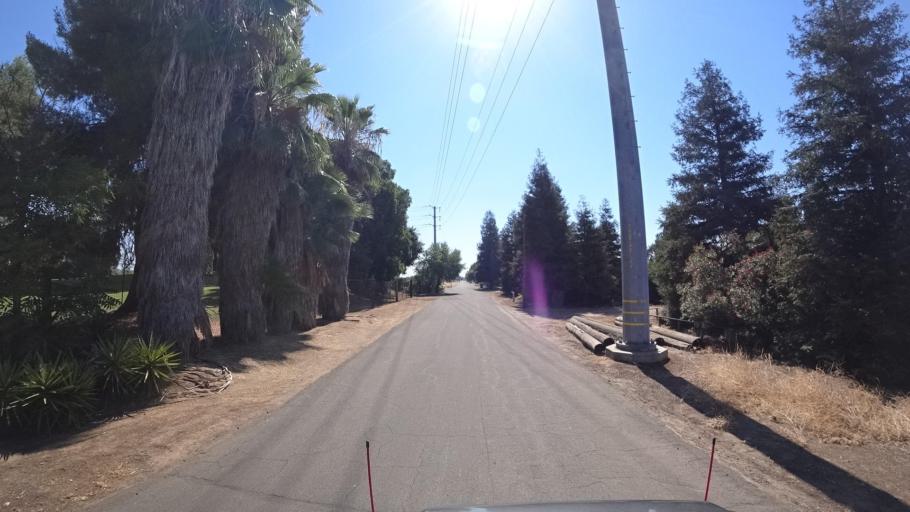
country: US
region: California
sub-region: Fresno County
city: Sunnyside
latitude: 36.7539
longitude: -119.6788
